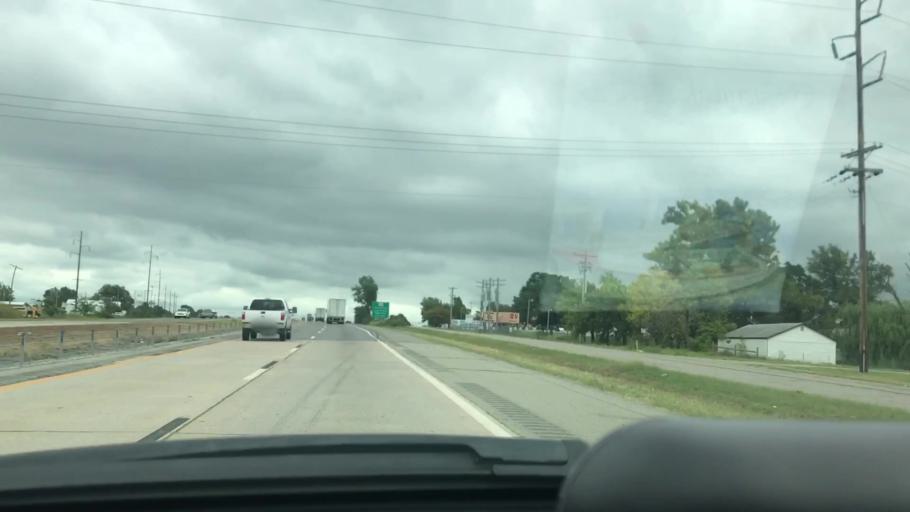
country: US
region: Oklahoma
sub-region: McIntosh County
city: Eufaula
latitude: 35.3556
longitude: -95.5757
